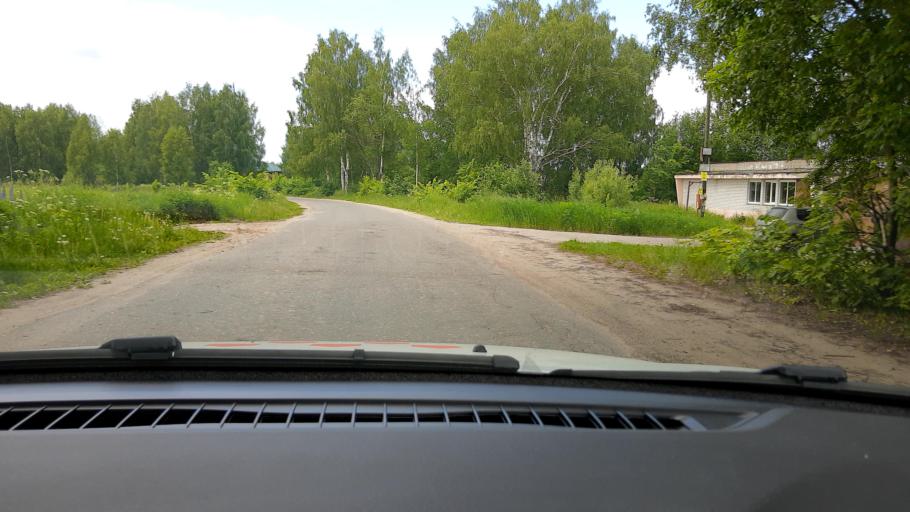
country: RU
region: Nizjnij Novgorod
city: Linda
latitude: 56.5362
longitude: 44.0916
